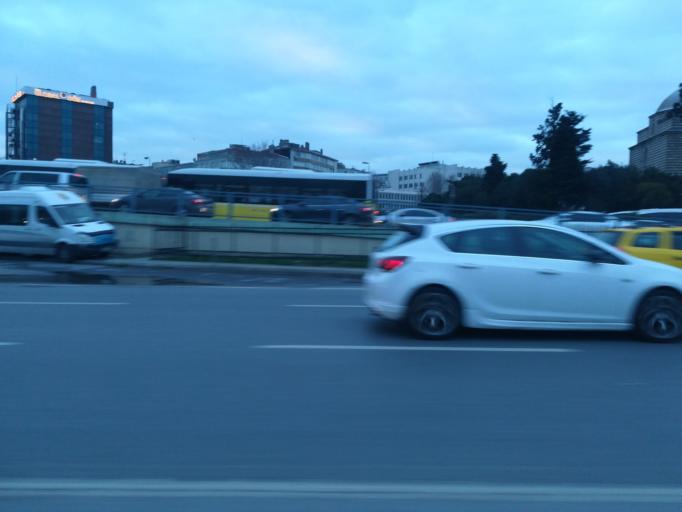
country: TR
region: Istanbul
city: Istanbul
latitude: 41.0105
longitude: 28.9501
